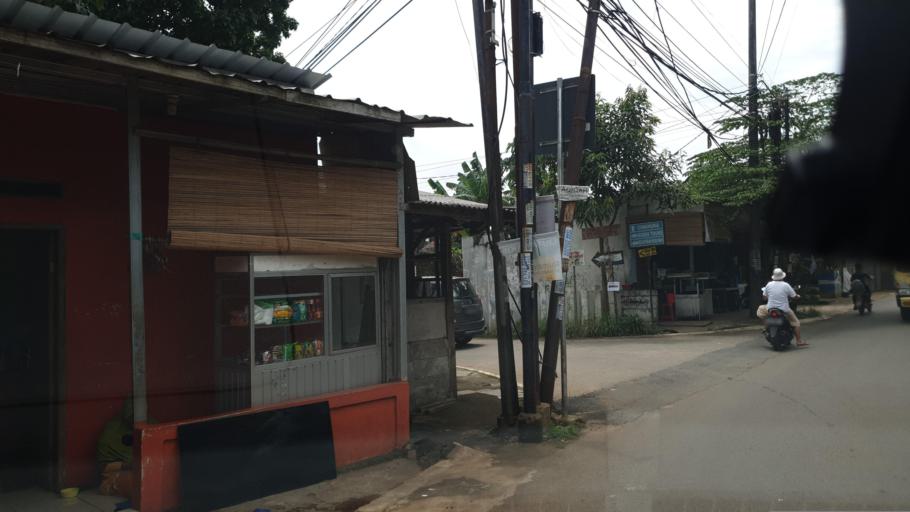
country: ID
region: West Java
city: Pamulang
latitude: -6.3670
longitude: 106.7623
